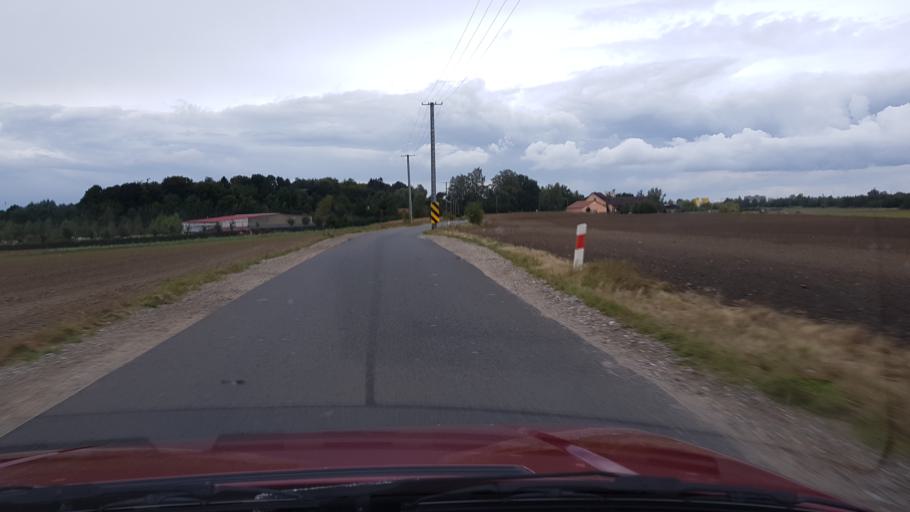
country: PL
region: West Pomeranian Voivodeship
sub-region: Koszalin
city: Koszalin
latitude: 54.1709
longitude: 16.1550
